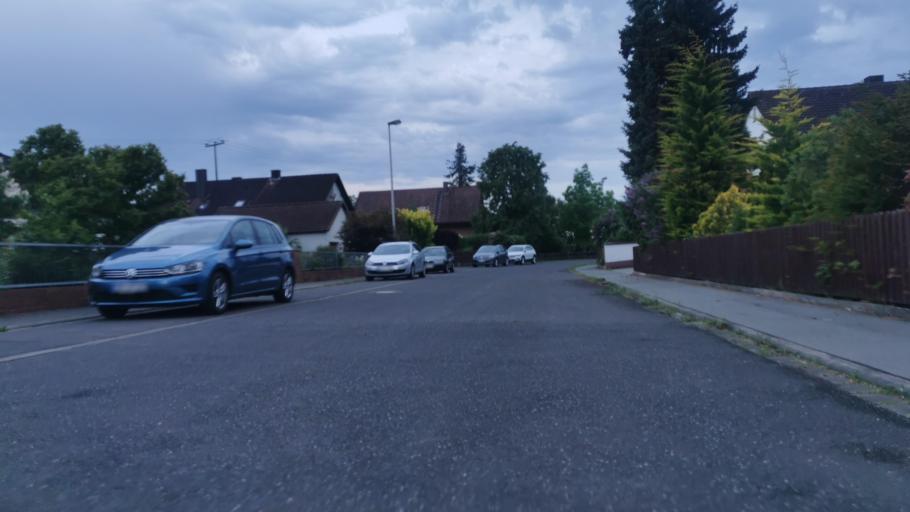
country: DE
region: Bavaria
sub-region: Regierungsbezirk Mittelfranken
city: Hochstadt an der Aisch
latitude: 49.7051
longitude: 10.8219
